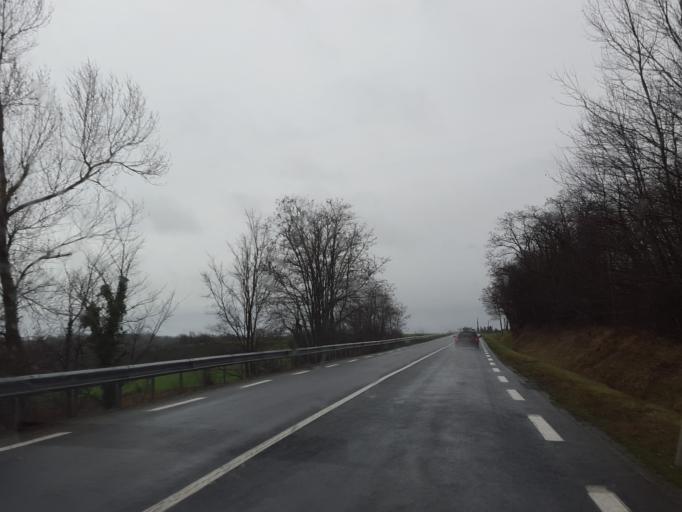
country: FR
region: Midi-Pyrenees
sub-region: Departement de l'Ariege
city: Mirepoix
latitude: 43.1382
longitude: 1.9556
